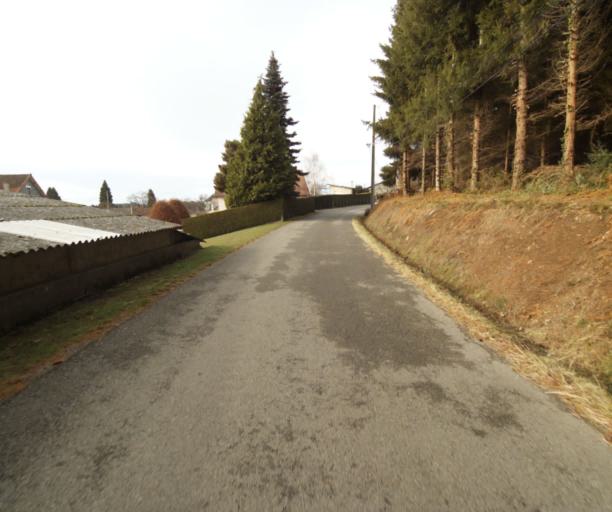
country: FR
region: Limousin
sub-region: Departement de la Correze
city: Saint-Mexant
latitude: 45.2727
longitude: 1.6821
